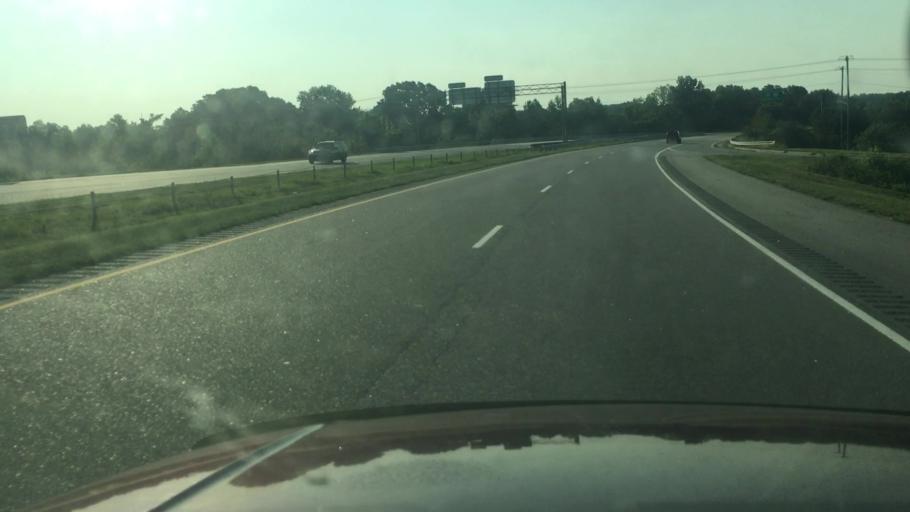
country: US
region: North Carolina
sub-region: Cumberland County
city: Fayetteville
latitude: 35.0379
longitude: -78.8854
